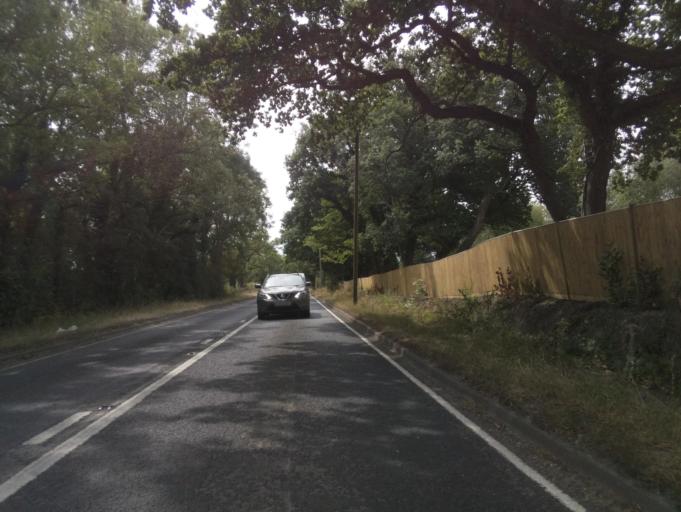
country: GB
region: England
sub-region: Surrey
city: Horley
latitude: 51.1780
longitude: -0.1950
